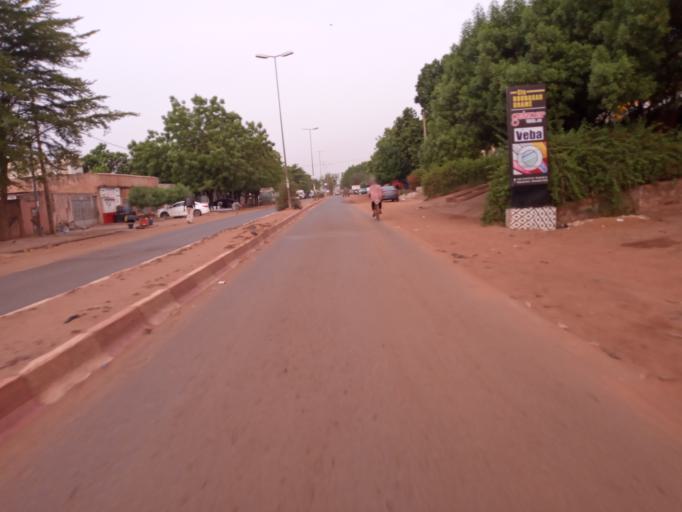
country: ML
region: Bamako
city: Bamako
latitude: 12.6628
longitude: -7.9741
